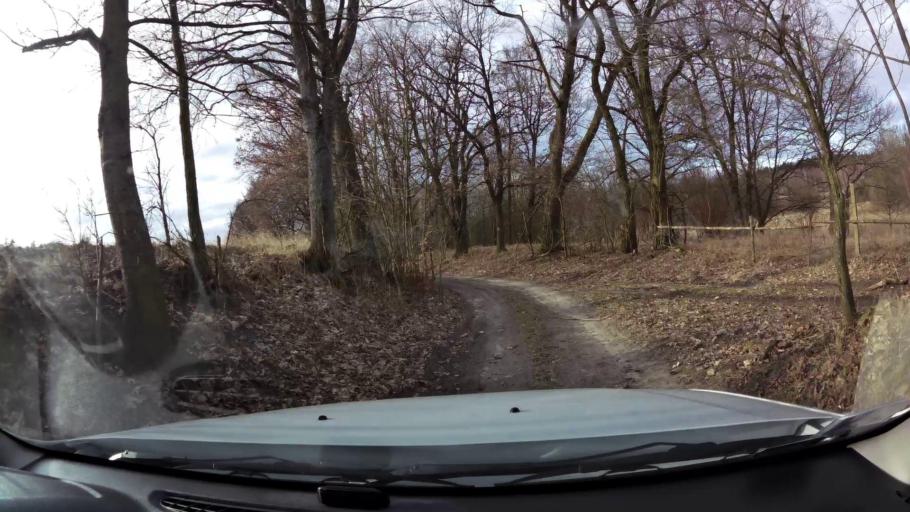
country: PL
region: West Pomeranian Voivodeship
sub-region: Powiat drawski
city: Drawsko Pomorskie
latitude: 53.5186
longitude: 15.7109
